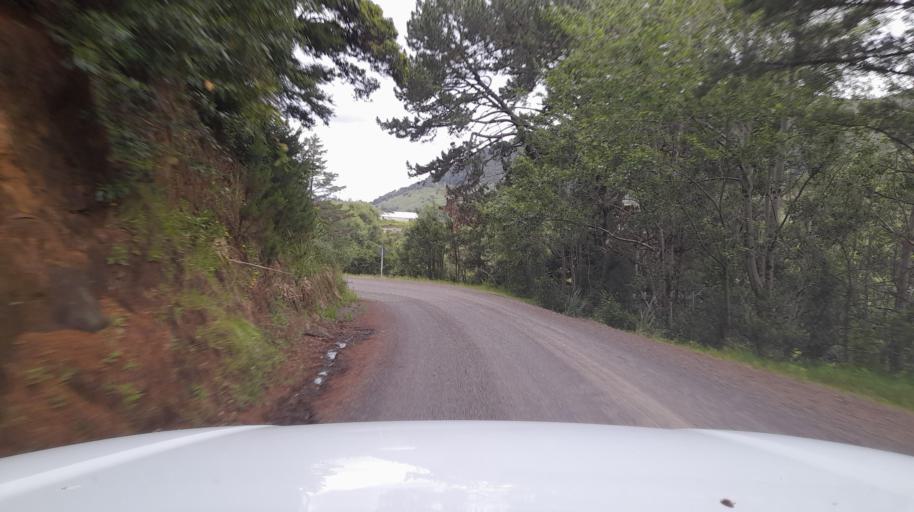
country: NZ
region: Northland
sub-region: Far North District
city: Kaitaia
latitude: -35.3288
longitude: 173.3537
